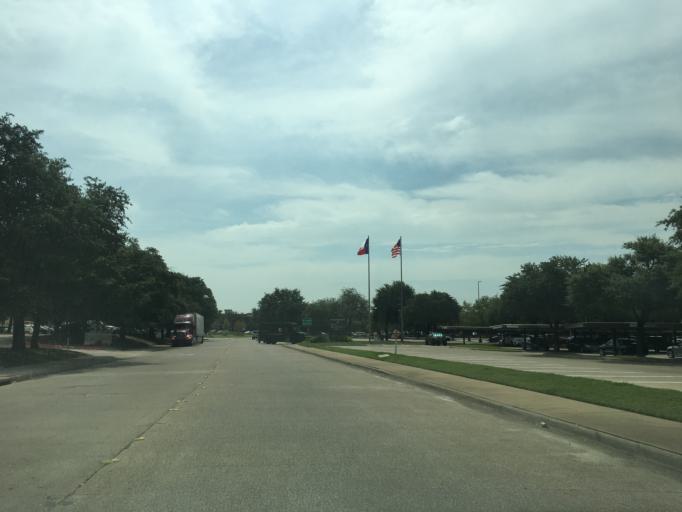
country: US
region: Texas
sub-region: Collin County
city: Plano
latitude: 33.0309
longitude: -96.7065
